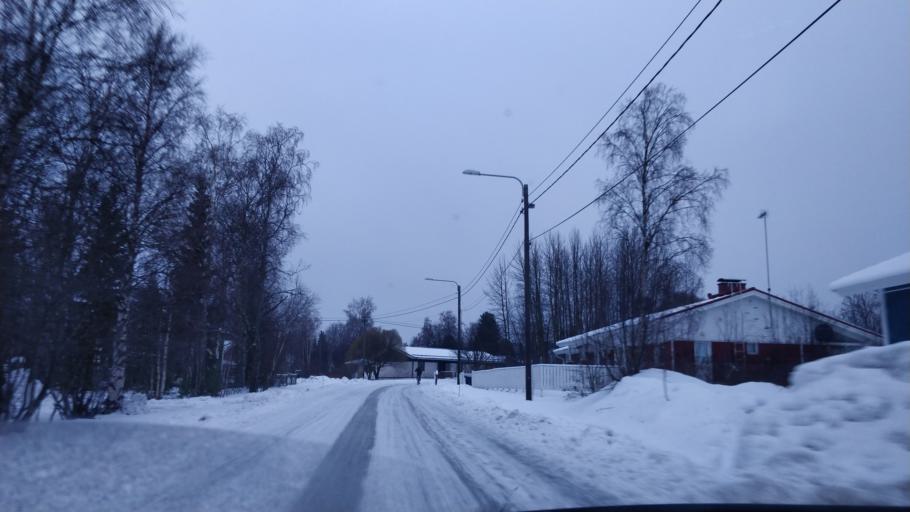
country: FI
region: Lapland
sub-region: Kemi-Tornio
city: Kemi
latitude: 65.7444
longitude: 24.5756
